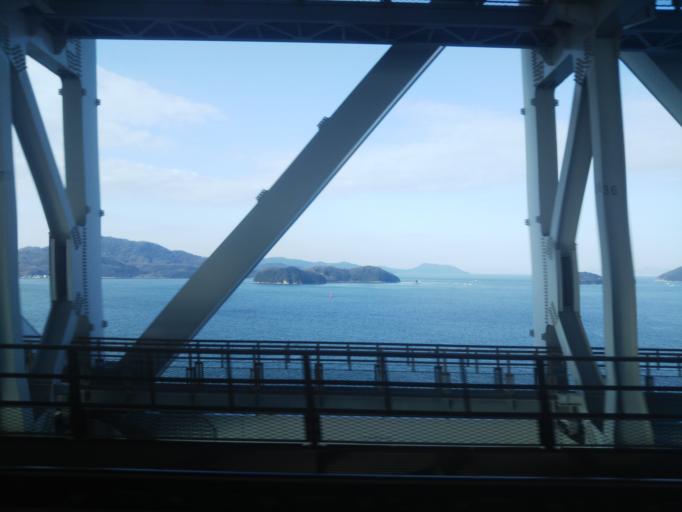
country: JP
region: Kagawa
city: Sakaidecho
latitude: 34.4101
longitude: 133.8069
